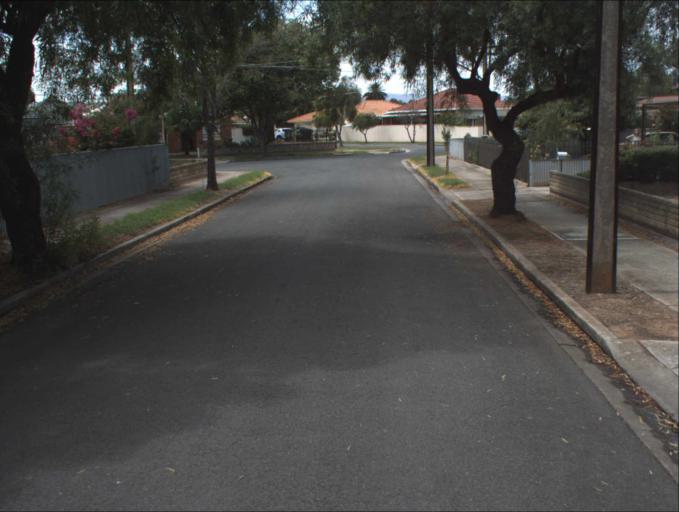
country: AU
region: South Australia
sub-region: Charles Sturt
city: Woodville
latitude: -34.8820
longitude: 138.5634
